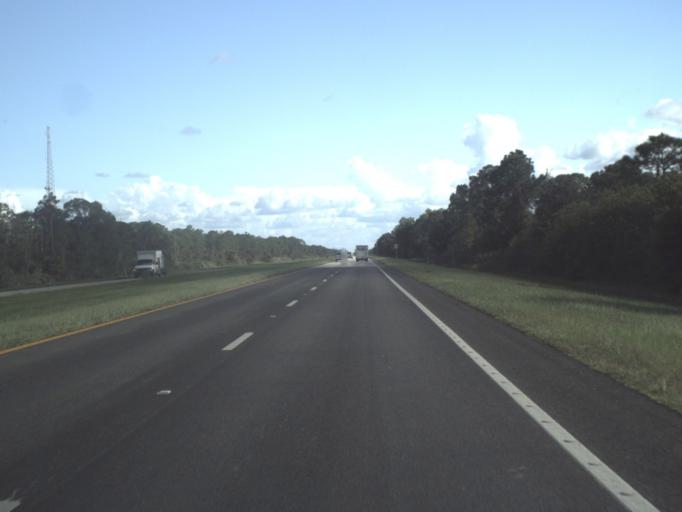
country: US
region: Florida
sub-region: Lee County
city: Burnt Store Marina
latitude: 26.8335
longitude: -81.9721
